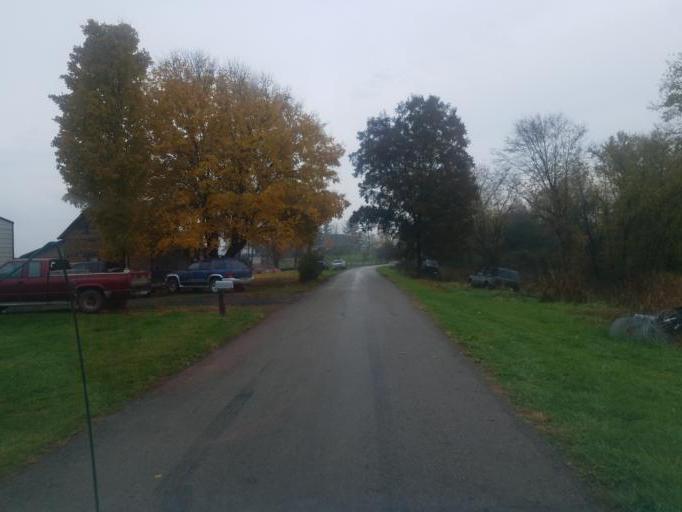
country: US
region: Ohio
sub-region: Morgan County
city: McConnelsville
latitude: 39.4966
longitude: -81.8084
